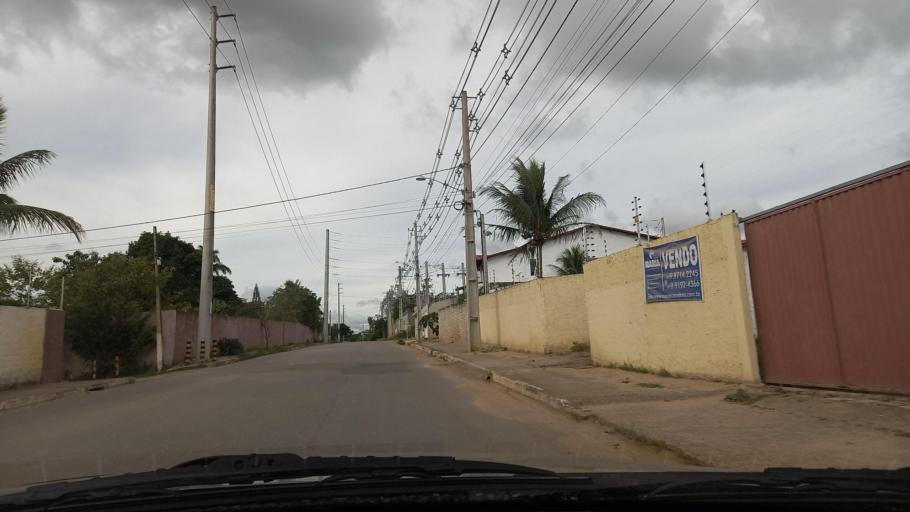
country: BR
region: Pernambuco
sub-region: Gravata
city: Gravata
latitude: -8.2003
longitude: -35.5447
